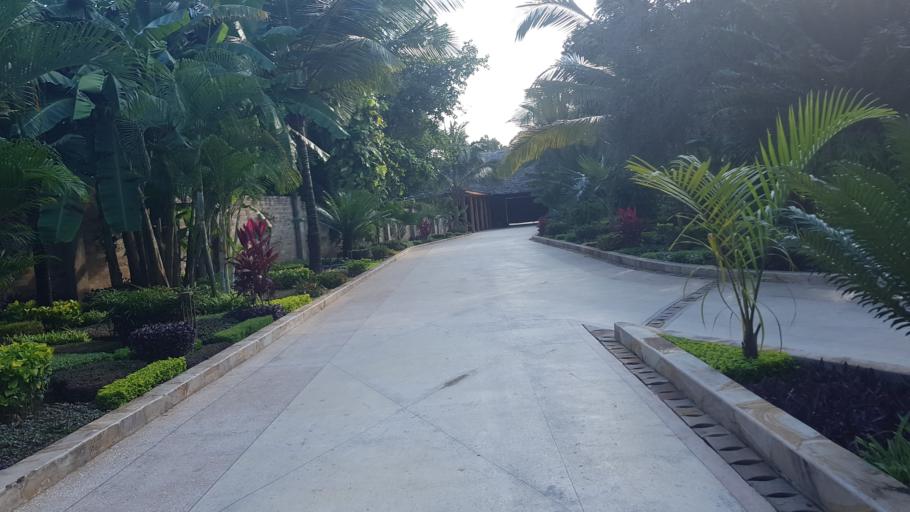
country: TZ
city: Kiwengwa
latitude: -6.0347
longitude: 39.4067
